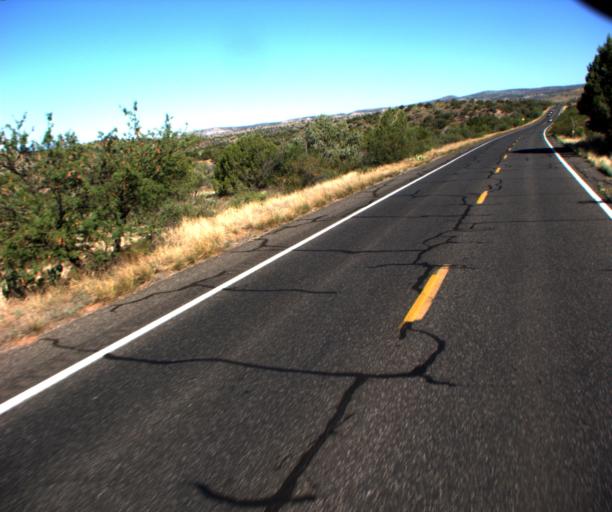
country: US
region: Arizona
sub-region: Yavapai County
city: Lake Montezuma
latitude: 34.7051
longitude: -111.7710
